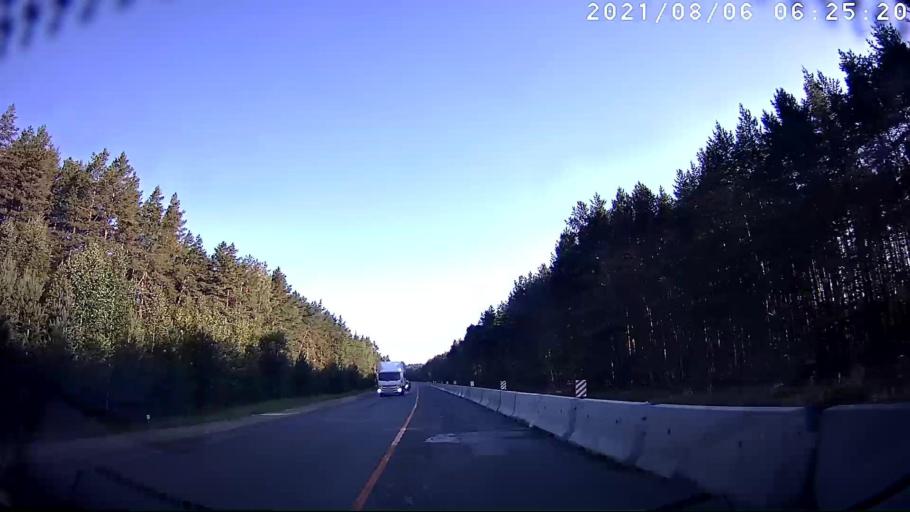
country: RU
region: Mariy-El
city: Krasnogorskiy
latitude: 56.1168
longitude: 48.3455
